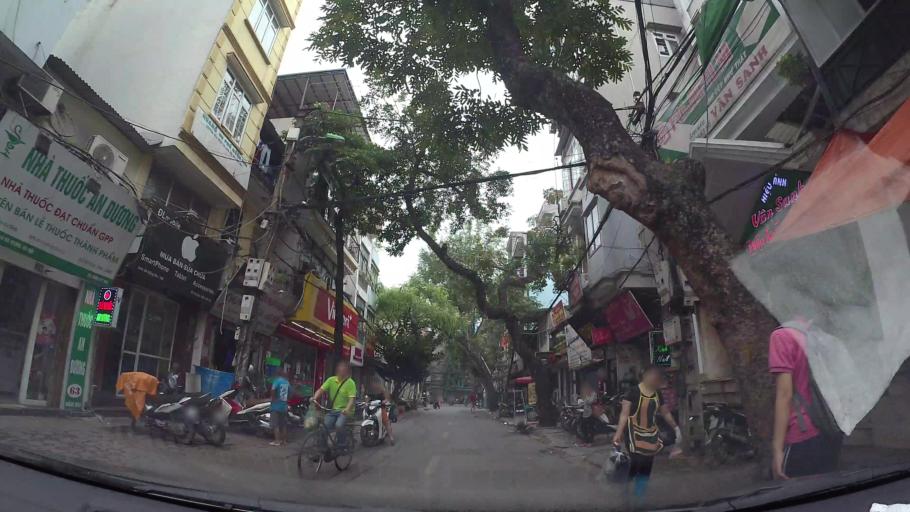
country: VN
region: Ha Noi
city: Hai BaTrung
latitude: 20.9986
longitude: 105.8522
